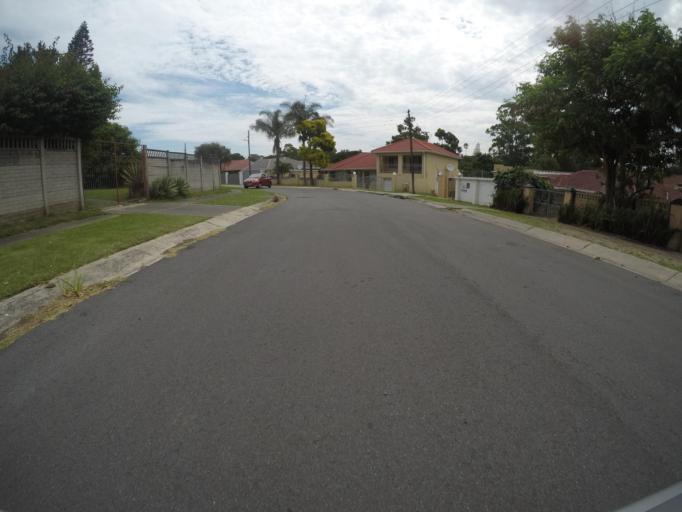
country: ZA
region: Eastern Cape
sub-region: Buffalo City Metropolitan Municipality
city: East London
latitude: -32.9919
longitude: 27.8777
